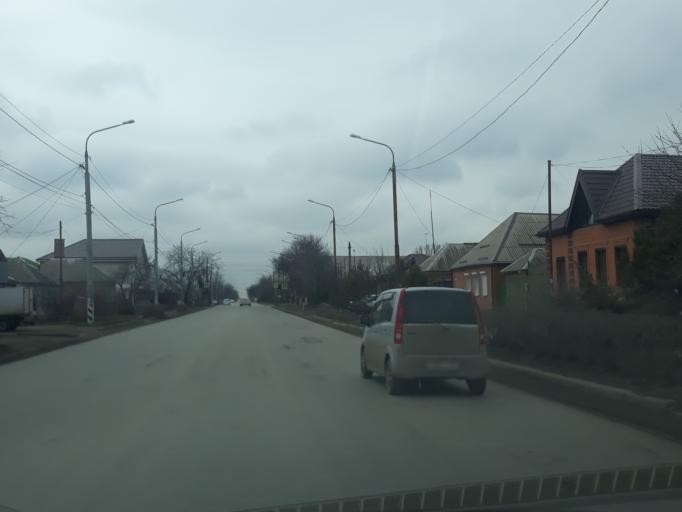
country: RU
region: Rostov
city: Taganrog
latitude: 47.2739
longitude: 38.9098
